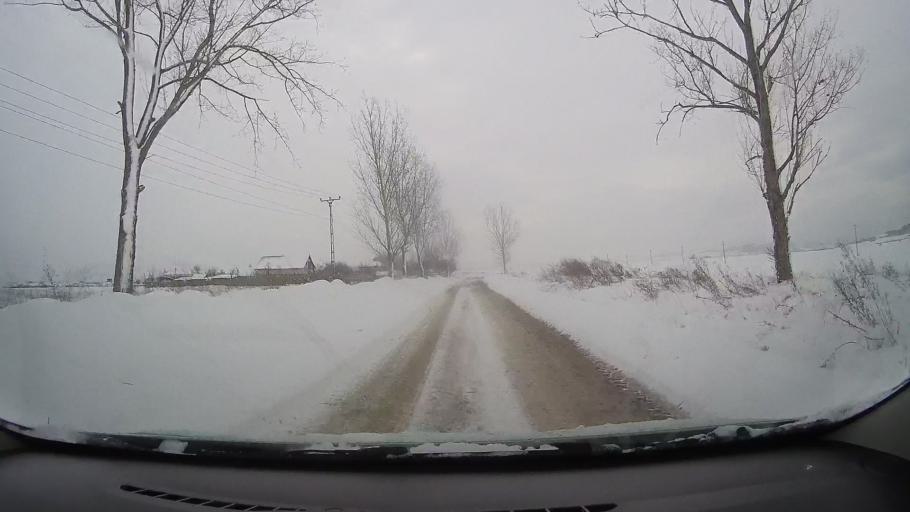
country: RO
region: Alba
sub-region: Comuna Pianu
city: Pianu de Jos
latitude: 45.9611
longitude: 23.5111
